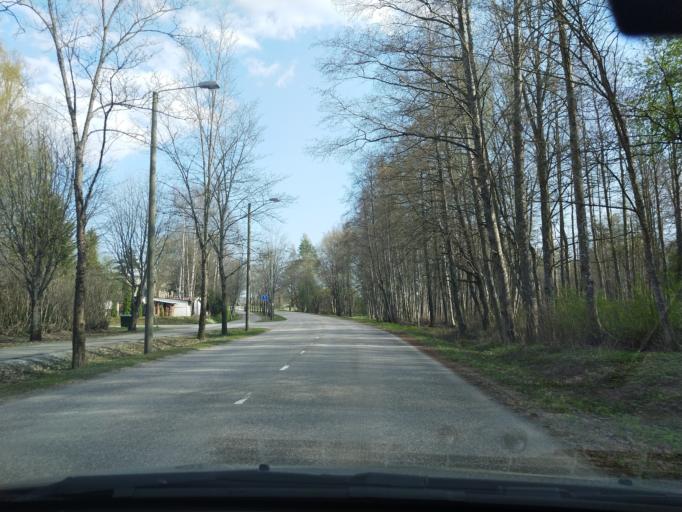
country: FI
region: Uusimaa
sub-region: Helsinki
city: Lohja
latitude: 60.1812
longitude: 23.9889
